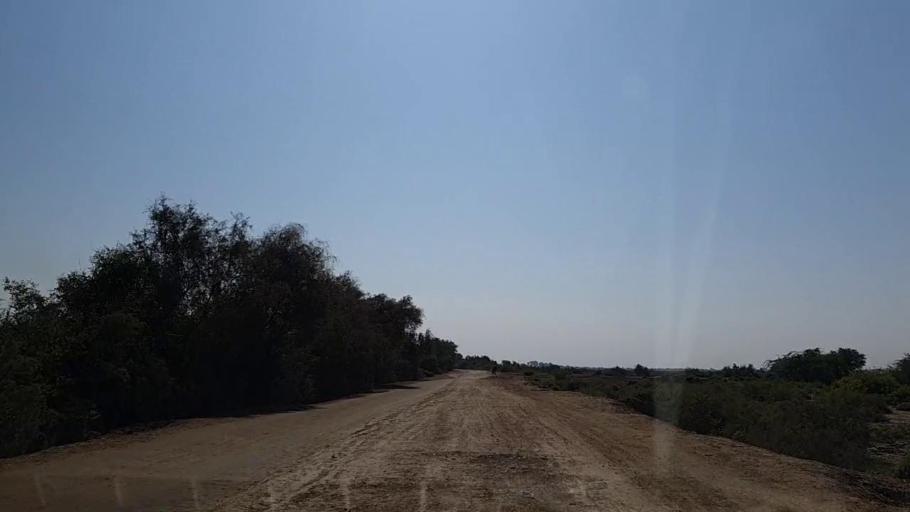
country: PK
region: Sindh
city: Chuhar Jamali
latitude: 24.5154
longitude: 68.0955
